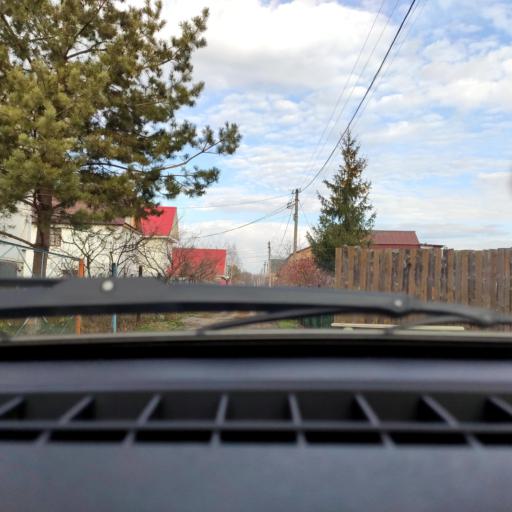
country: RU
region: Bashkortostan
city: Ufa
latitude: 54.6310
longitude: 55.8911
